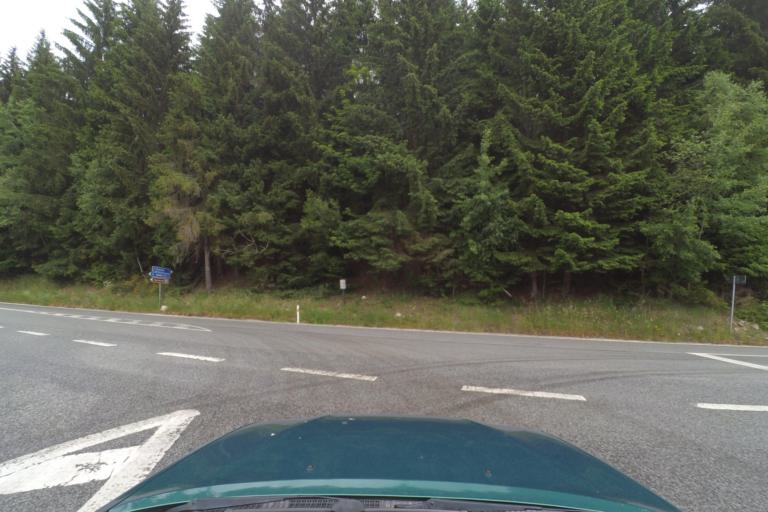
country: CZ
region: Liberecky
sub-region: Okres Jablonec nad Nisou
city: Korenov
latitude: 50.7623
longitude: 15.3978
